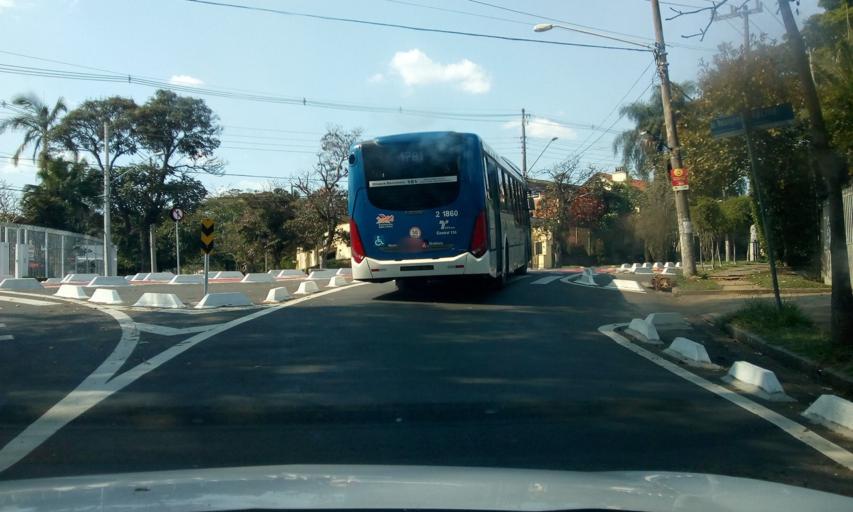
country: BR
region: Sao Paulo
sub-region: Osasco
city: Osasco
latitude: -23.5251
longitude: -46.7236
